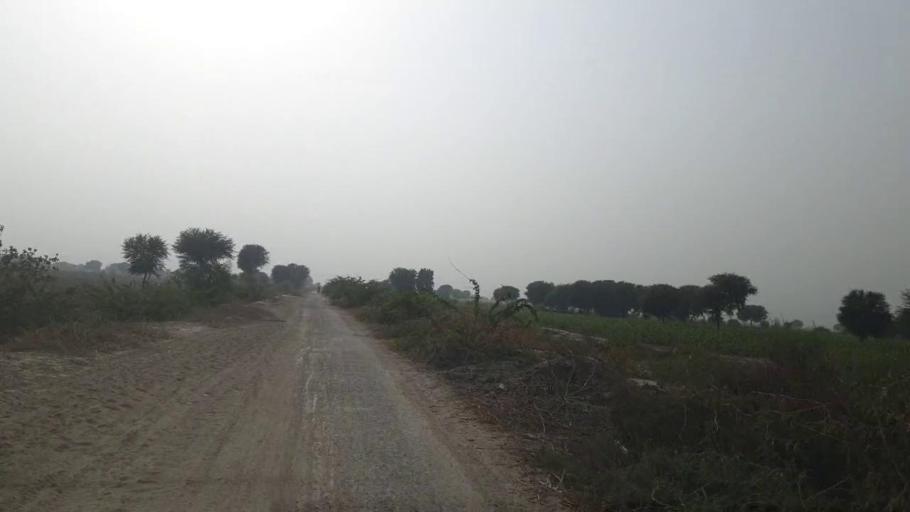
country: PK
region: Sindh
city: Kunri
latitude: 25.0715
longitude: 69.5054
